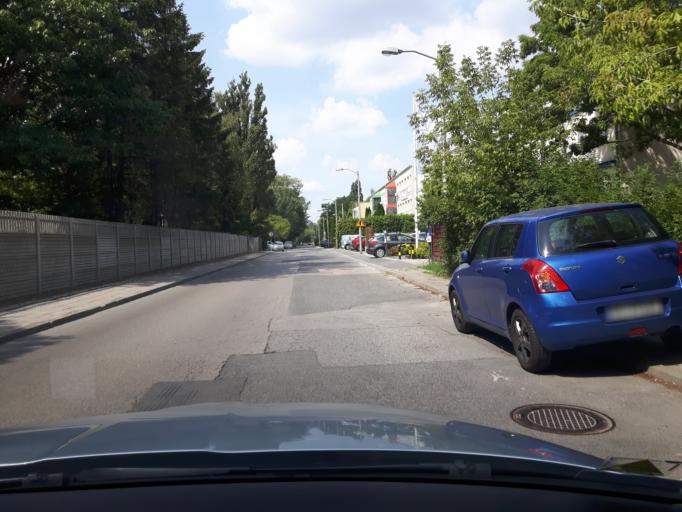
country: PL
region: Masovian Voivodeship
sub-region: Warszawa
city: Mokotow
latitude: 52.1649
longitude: 20.9979
